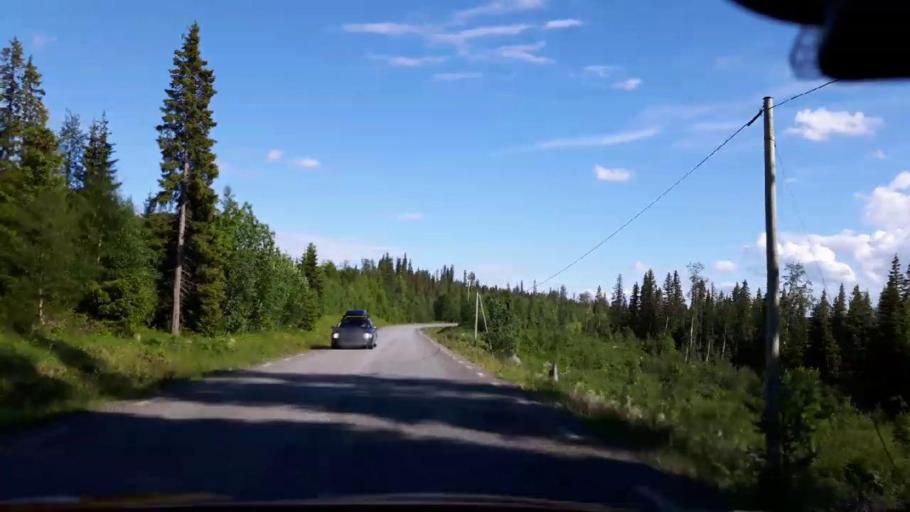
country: SE
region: Jaemtland
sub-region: Krokoms Kommun
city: Valla
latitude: 63.7106
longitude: 14.1387
